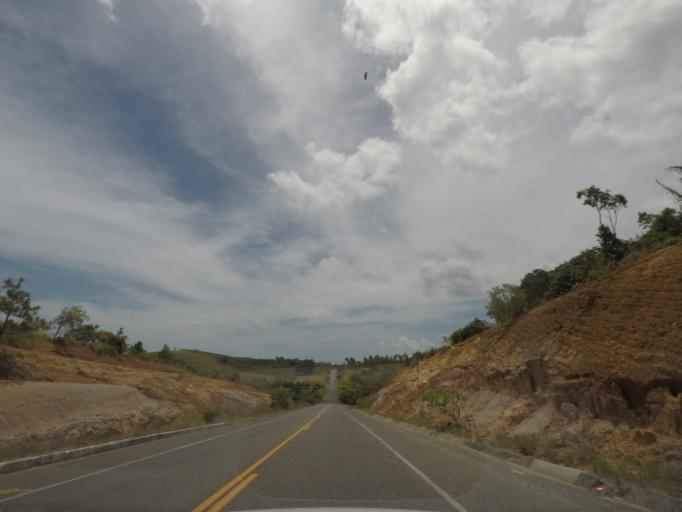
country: BR
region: Bahia
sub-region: Conde
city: Conde
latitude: -11.8818
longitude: -37.6490
